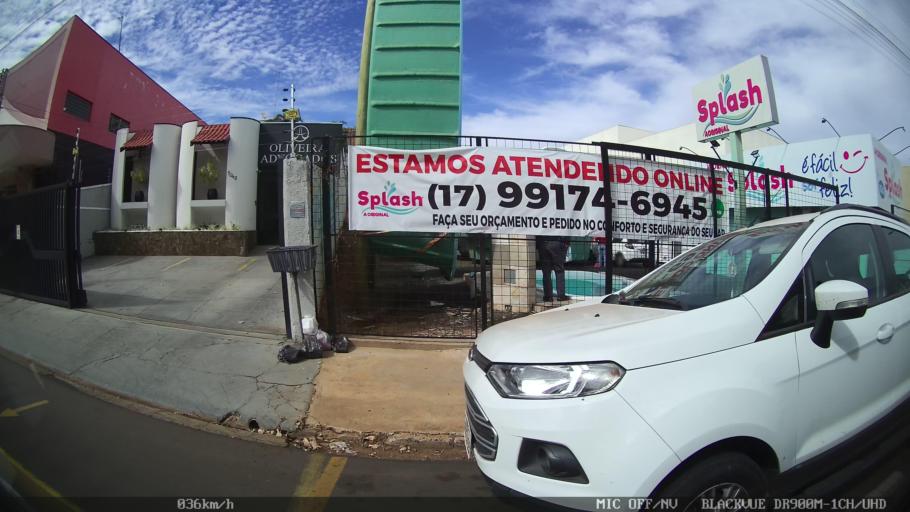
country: BR
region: Sao Paulo
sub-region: Catanduva
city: Catanduva
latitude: -21.1455
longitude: -48.9728
